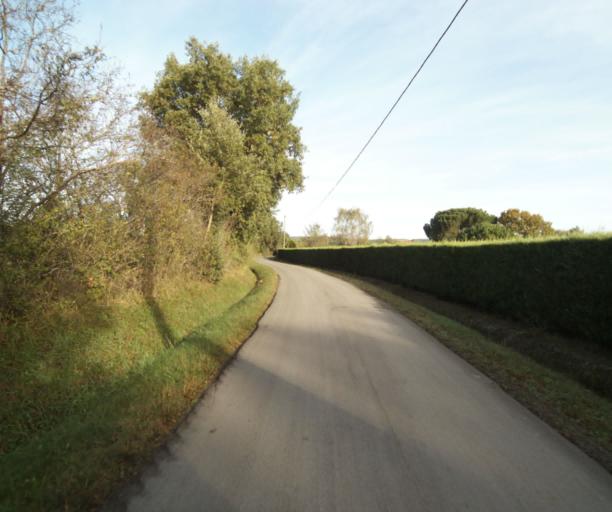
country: FR
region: Midi-Pyrenees
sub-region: Departement de la Haute-Garonne
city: Villemur-sur-Tarn
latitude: 43.9236
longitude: 1.5058
